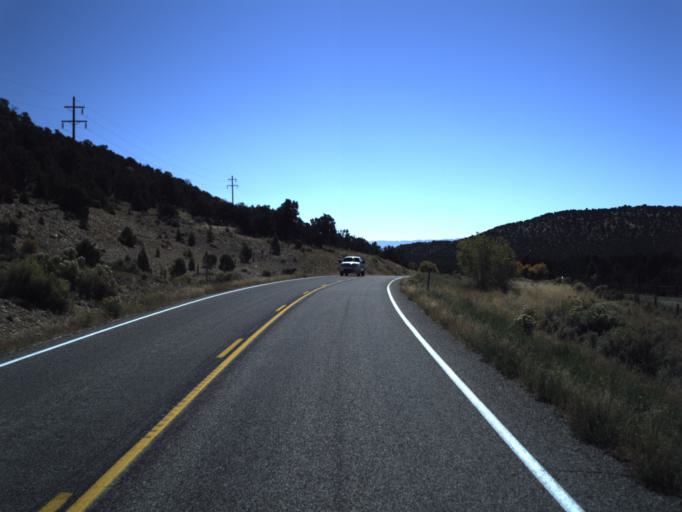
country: US
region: Utah
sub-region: Wayne County
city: Loa
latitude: 37.9368
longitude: -111.4314
